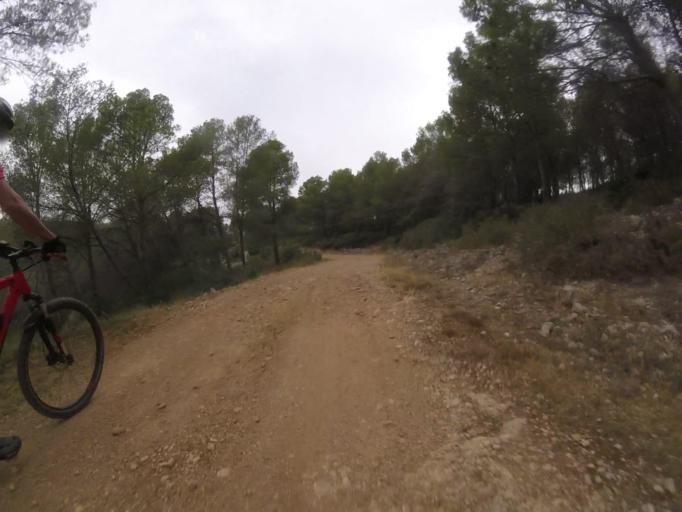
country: ES
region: Valencia
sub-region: Provincia de Castello
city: Alcala de Xivert
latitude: 40.3172
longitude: 0.2719
